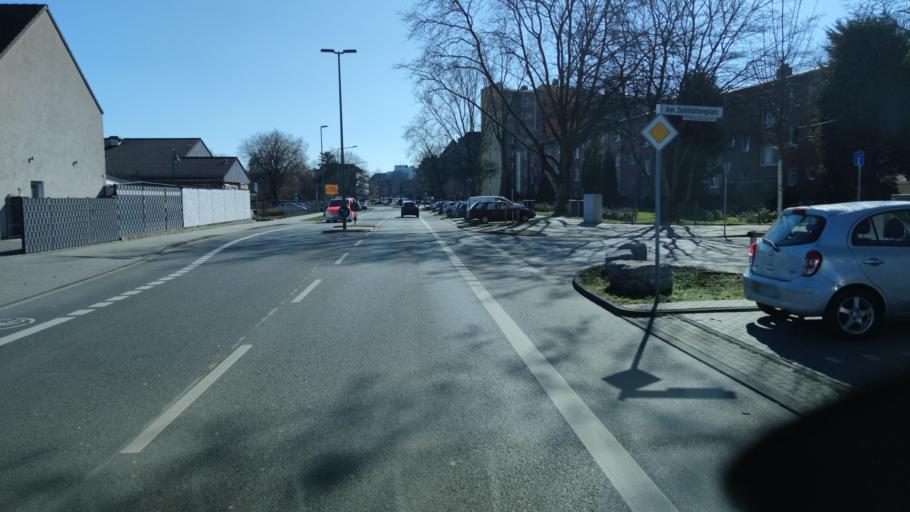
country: DE
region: North Rhine-Westphalia
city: Meiderich
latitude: 51.5012
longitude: 6.7695
